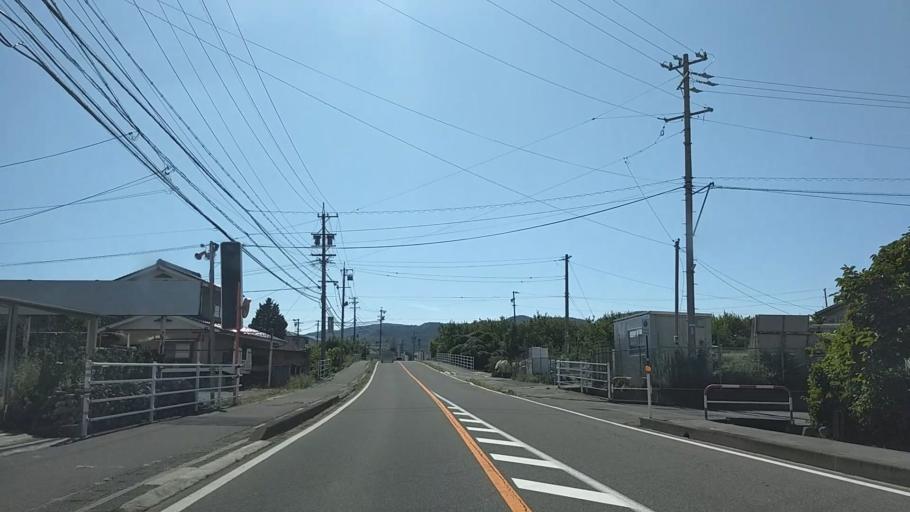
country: JP
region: Nagano
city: Nagano-shi
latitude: 36.6256
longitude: 138.1515
